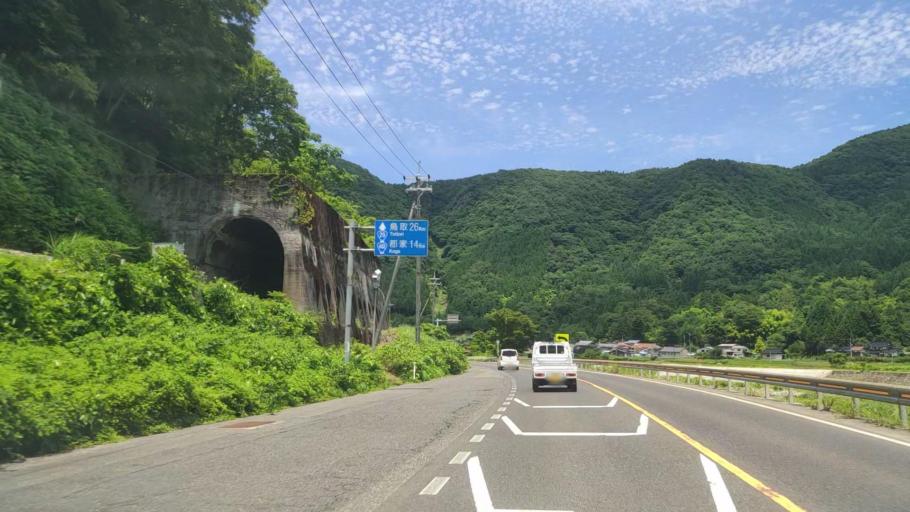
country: JP
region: Tottori
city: Tottori
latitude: 35.3652
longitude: 134.3779
